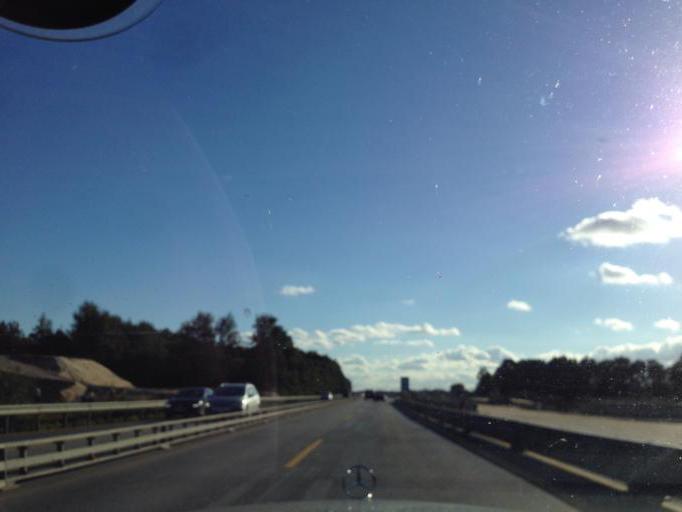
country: DE
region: Schleswig-Holstein
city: Krogaspe
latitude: 54.0979
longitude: 9.9348
